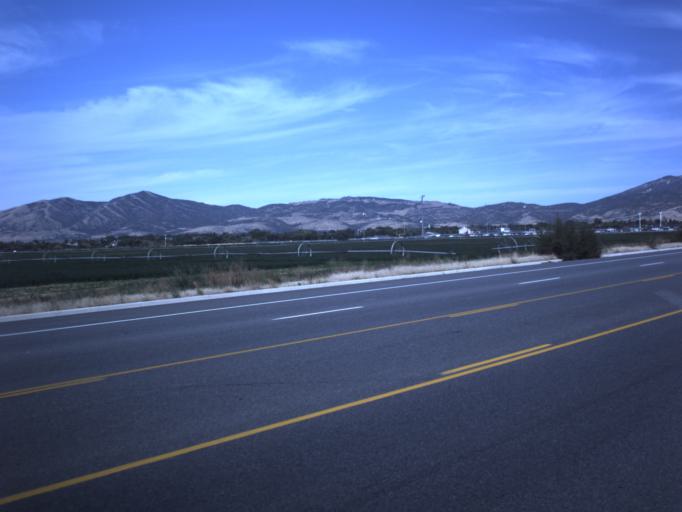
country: US
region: Utah
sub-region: Utah County
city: Cedar Hills
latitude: 40.4107
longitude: -111.7734
